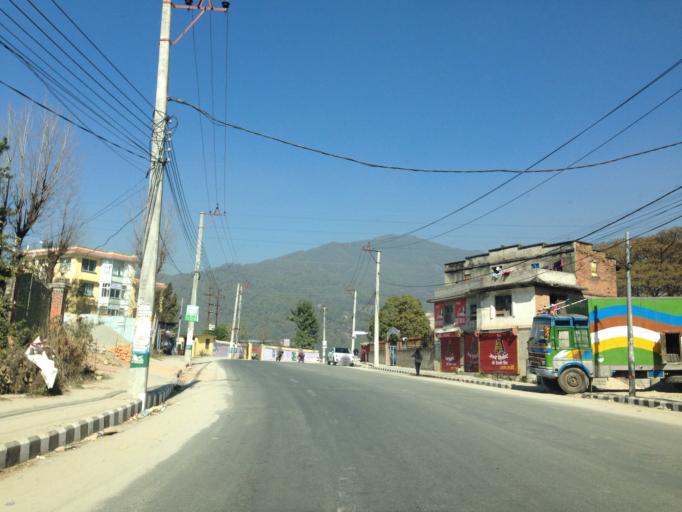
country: NP
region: Central Region
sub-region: Bagmati Zone
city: Kathmandu
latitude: 27.7649
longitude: 85.3537
